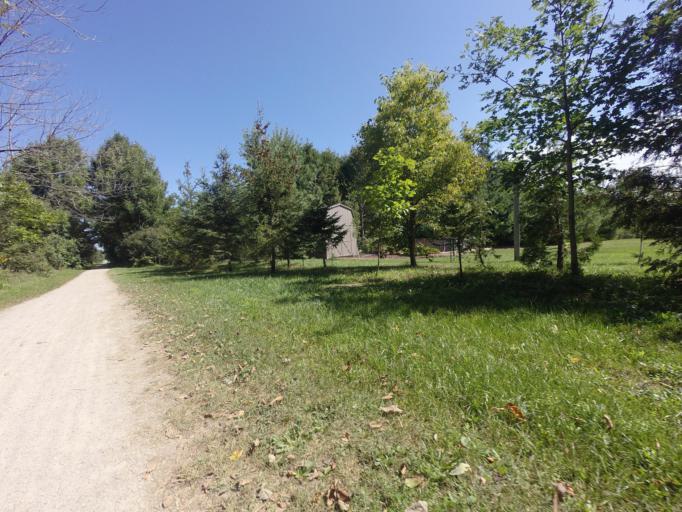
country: CA
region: Ontario
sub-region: Wellington County
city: Guelph
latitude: 43.7272
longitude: -80.3704
